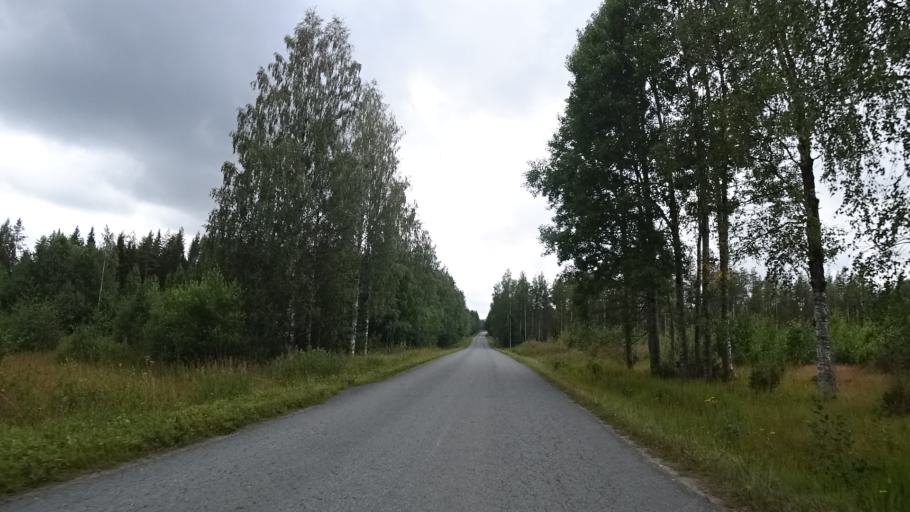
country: FI
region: North Karelia
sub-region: Joensuu
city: Ilomantsi
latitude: 62.9412
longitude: 31.2895
